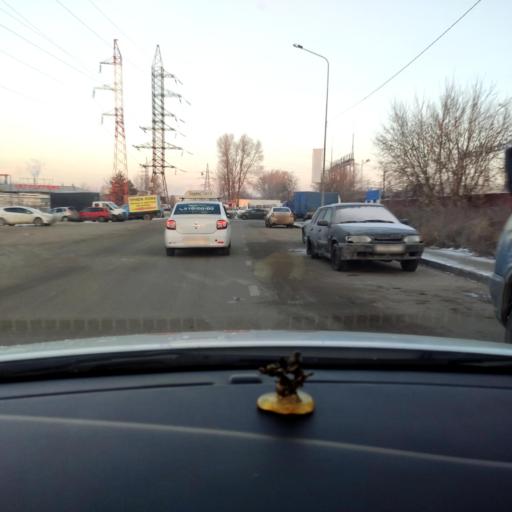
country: RU
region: Tatarstan
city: Staroye Arakchino
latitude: 55.8294
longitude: 49.0308
